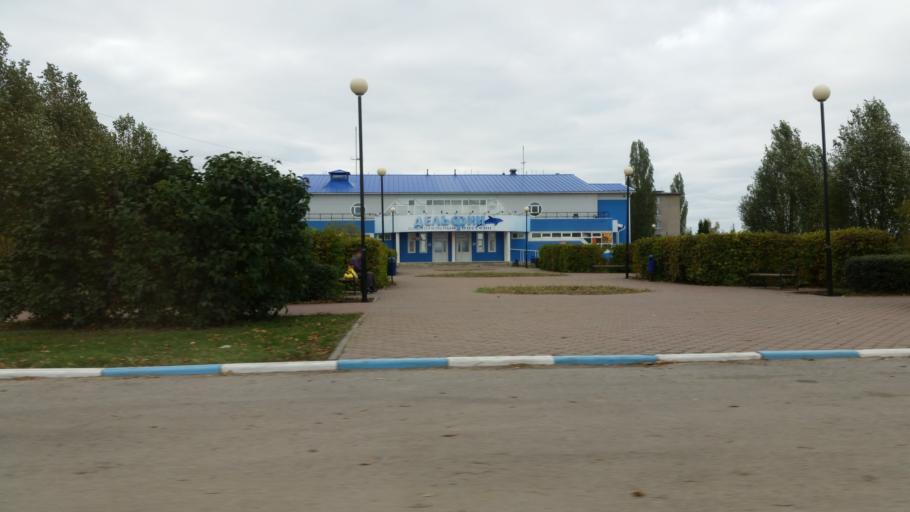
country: RU
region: Lipetsk
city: Gryazi
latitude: 52.4749
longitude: 39.9473
